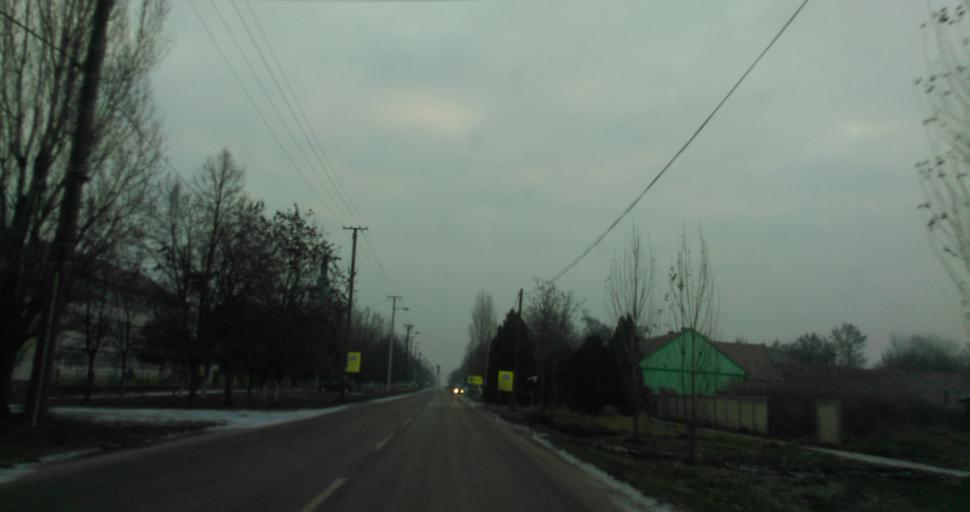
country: RS
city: Kumane
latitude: 45.5366
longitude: 20.2255
